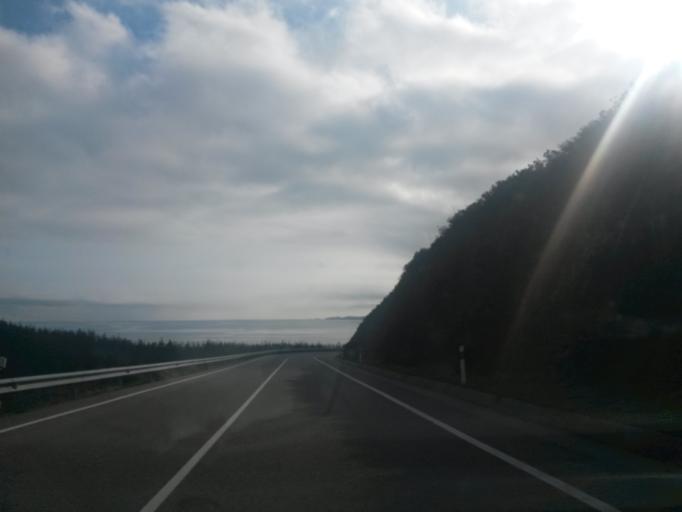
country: ES
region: Catalonia
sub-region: Provincia de Girona
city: Colera
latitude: 42.4120
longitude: 3.1542
